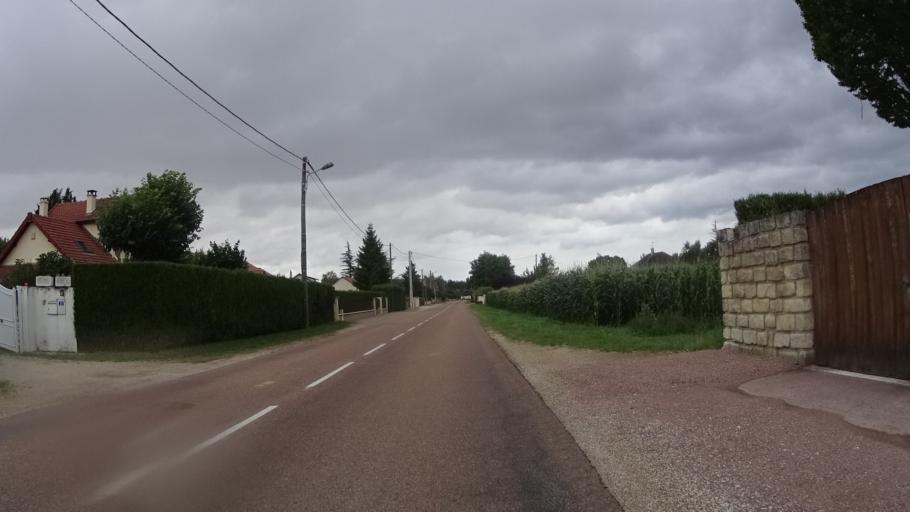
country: FR
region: Champagne-Ardenne
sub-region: Departement de l'Aube
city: Verrieres
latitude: 48.2468
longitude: 4.1864
